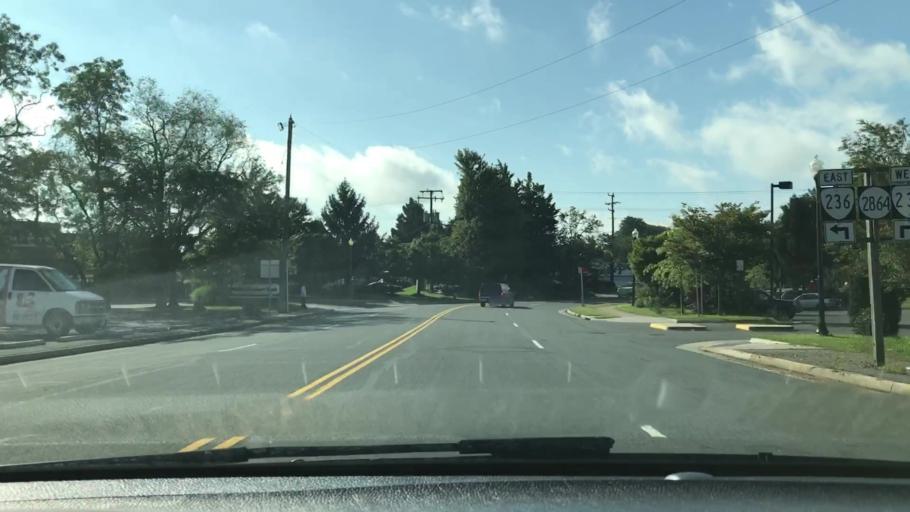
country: US
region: Virginia
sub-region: Fairfax County
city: Annandale
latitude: 38.8317
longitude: -77.1966
